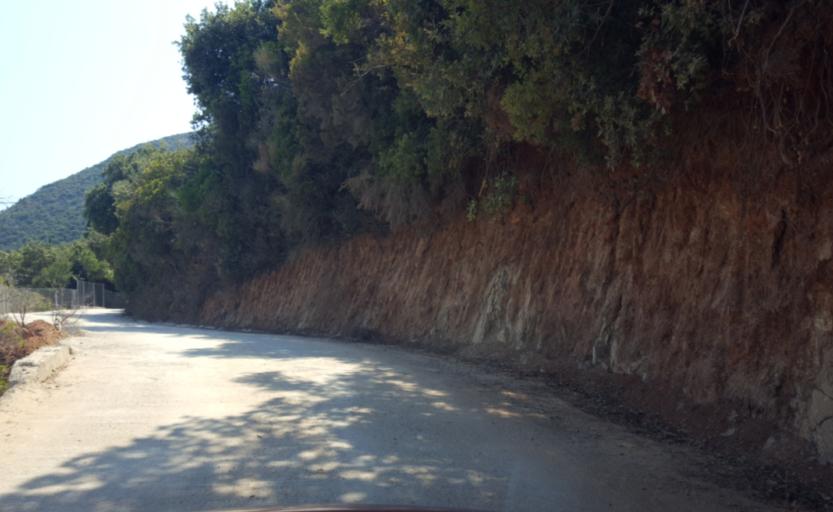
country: GR
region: Ionian Islands
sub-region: Lefkada
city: Nidri
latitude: 38.6589
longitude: 20.7172
